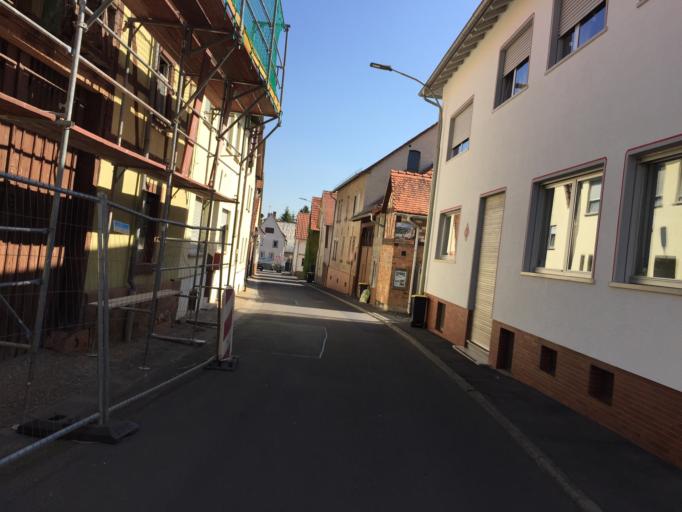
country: DE
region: Hesse
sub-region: Regierungsbezirk Giessen
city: Hungen
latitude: 50.4467
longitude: 8.9038
